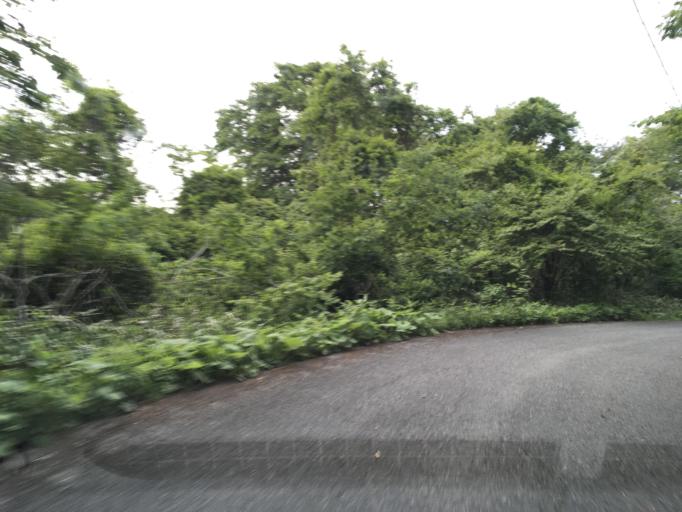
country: JP
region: Iwate
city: Mizusawa
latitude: 39.1388
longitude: 141.3035
